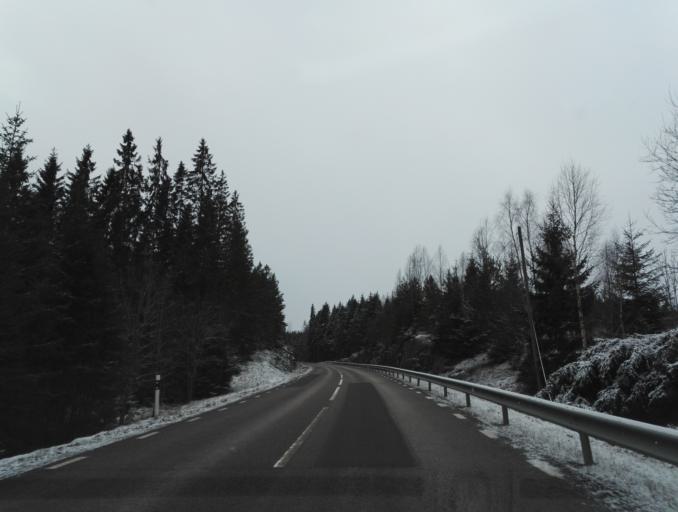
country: SE
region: Kalmar
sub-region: Hultsfreds Kommun
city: Virserum
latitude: 57.1922
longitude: 15.5058
